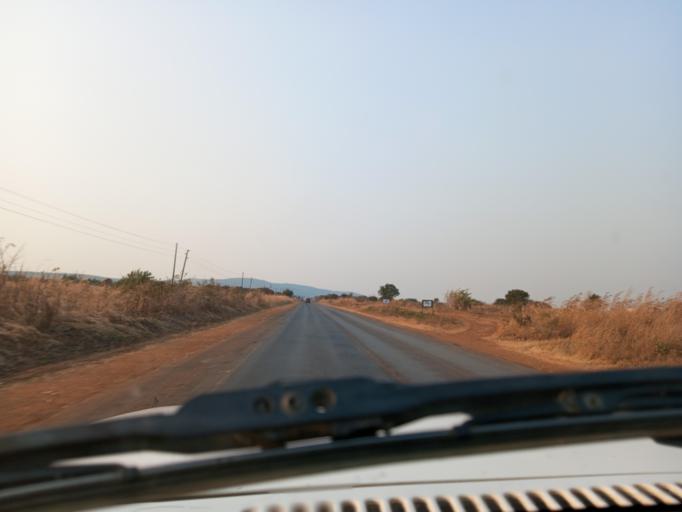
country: ZM
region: Northern
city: Mpika
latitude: -11.9123
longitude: 31.4159
